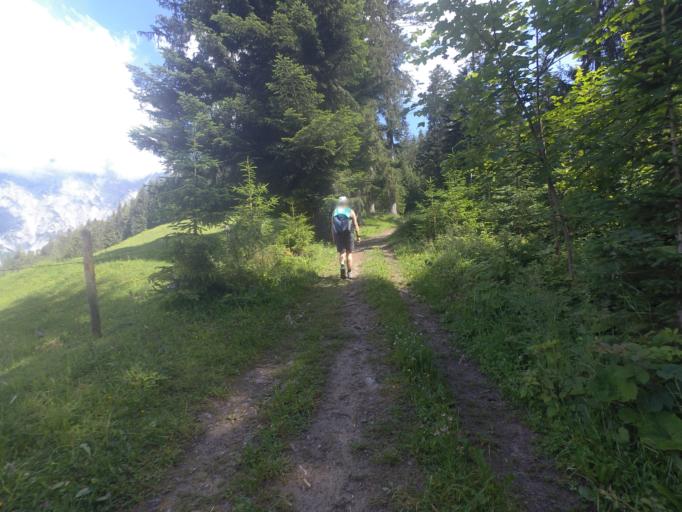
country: AT
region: Salzburg
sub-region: Politischer Bezirk Zell am See
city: Leogang
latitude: 47.4525
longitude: 12.7728
